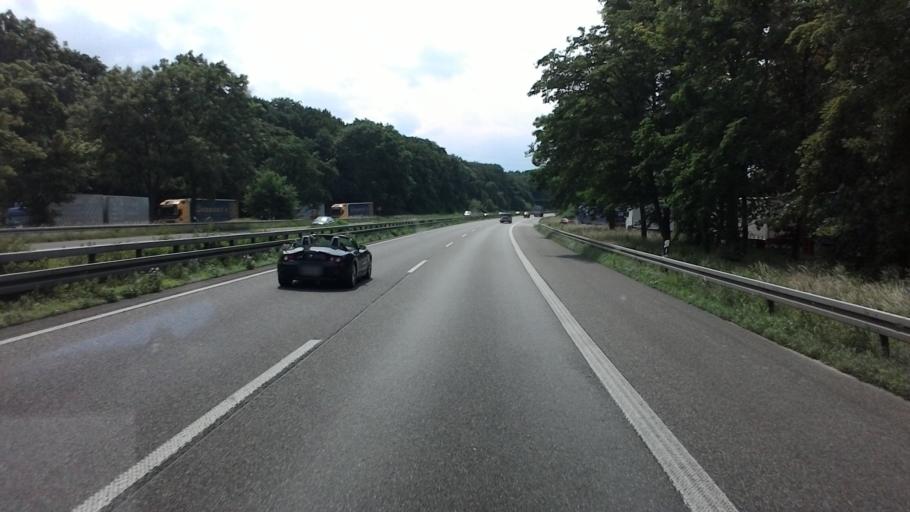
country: DE
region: North Rhine-Westphalia
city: Stolberg
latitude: 50.7681
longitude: 6.1729
